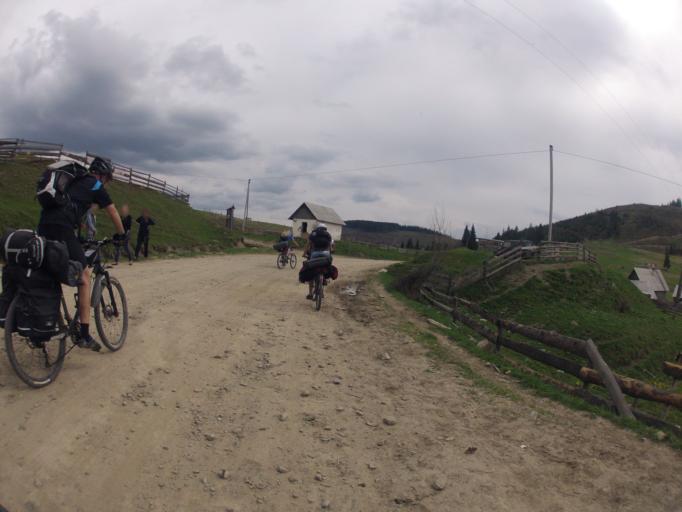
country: UA
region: Chernivtsi
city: Putyla
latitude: 47.8899
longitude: 25.1659
